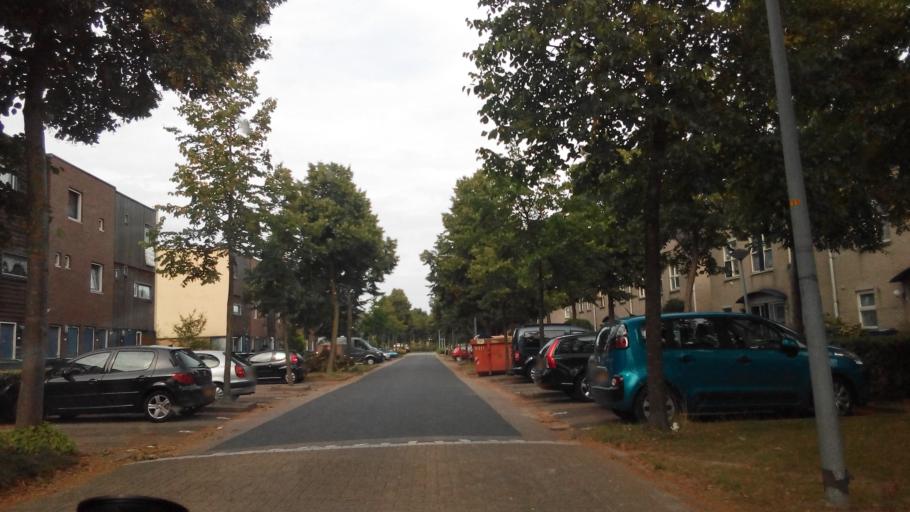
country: NL
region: Flevoland
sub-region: Gemeente Almere
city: Almere Stad
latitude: 52.3876
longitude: 5.2677
